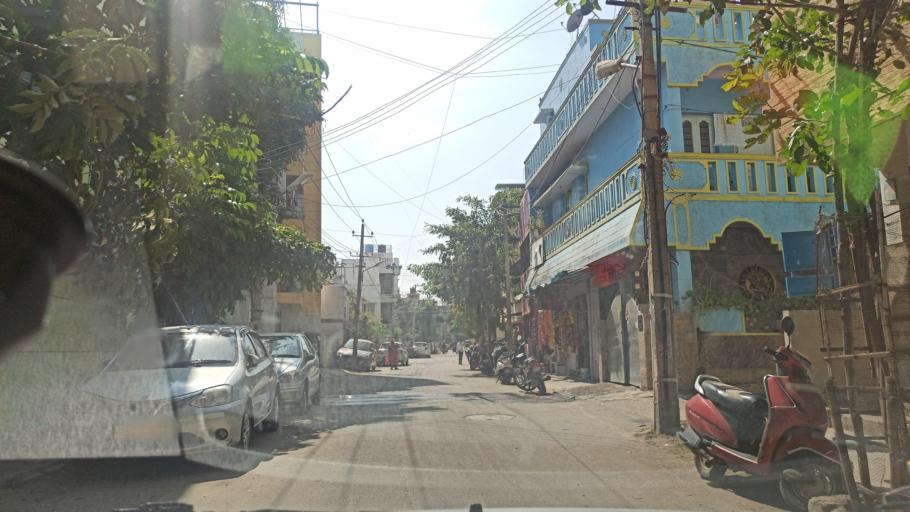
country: IN
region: Karnataka
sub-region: Bangalore Urban
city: Yelahanka
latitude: 13.0378
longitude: 77.5999
